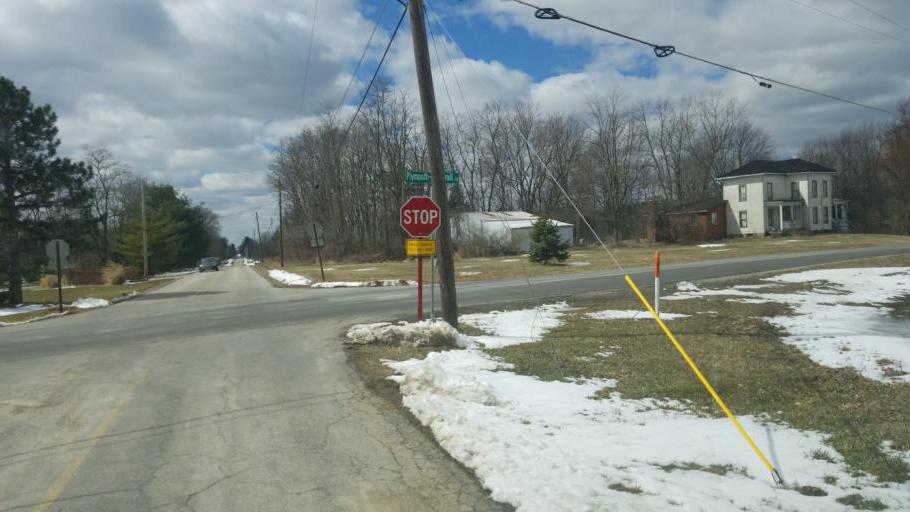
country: US
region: Ohio
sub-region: Richland County
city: Shelby
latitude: 40.8431
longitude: -82.6029
